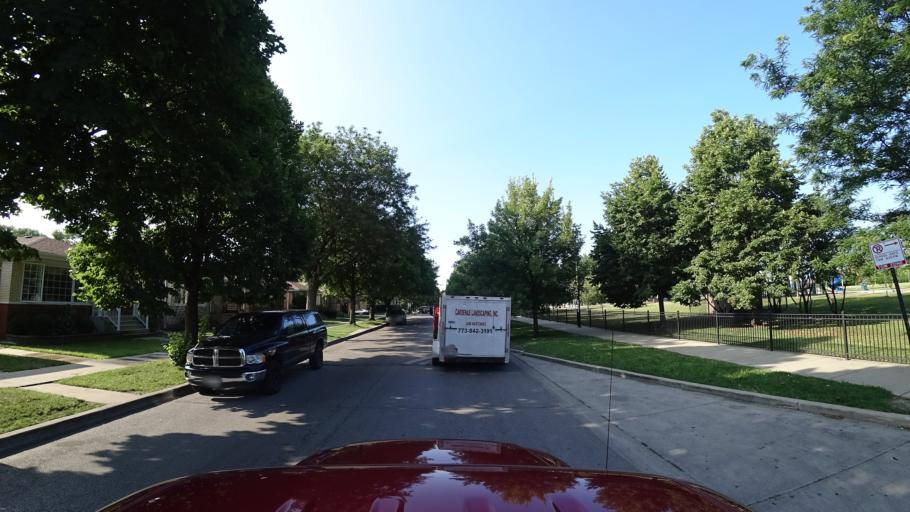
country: US
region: Illinois
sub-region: Cook County
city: Hometown
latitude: 41.7922
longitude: -87.7109
